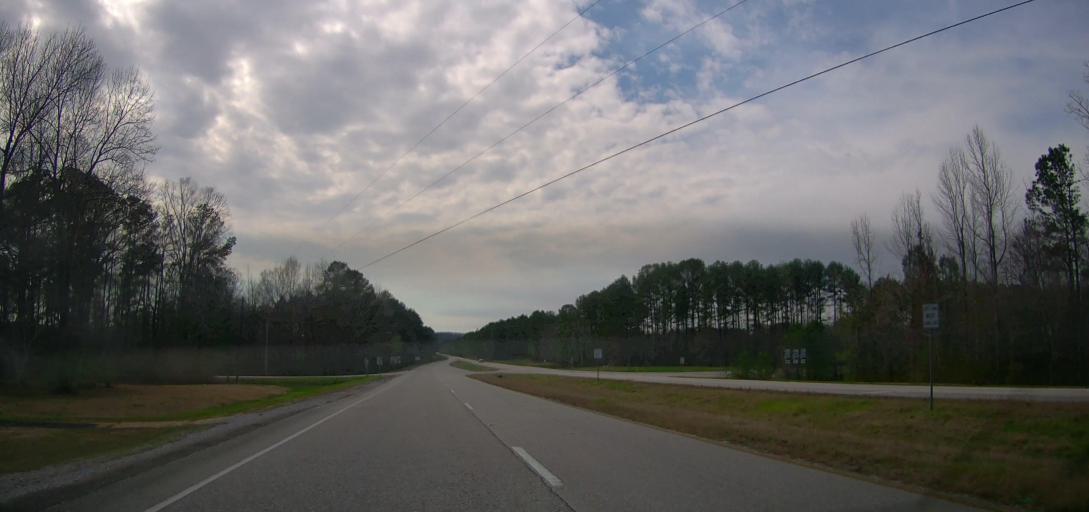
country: US
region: Alabama
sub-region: Marion County
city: Winfield
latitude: 33.9330
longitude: -87.7056
